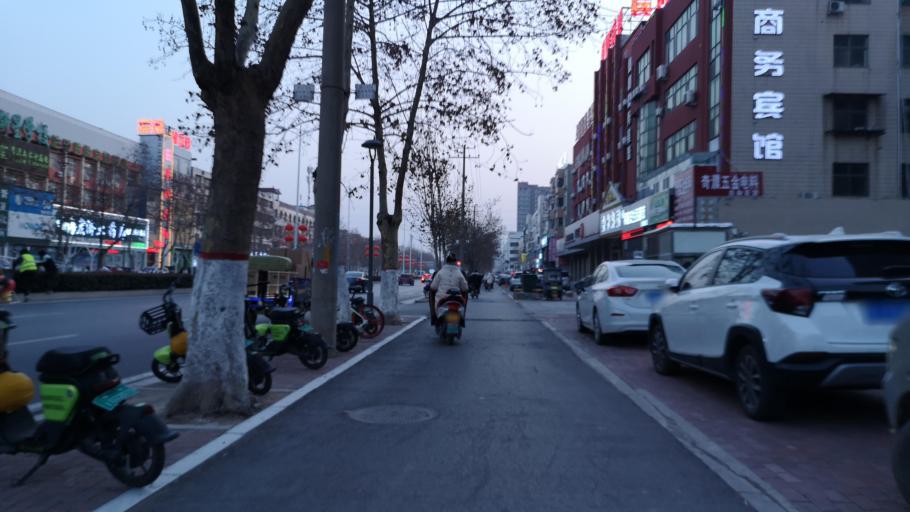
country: CN
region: Henan Sheng
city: Zhongyuanlu
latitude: 35.7679
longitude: 115.0688
